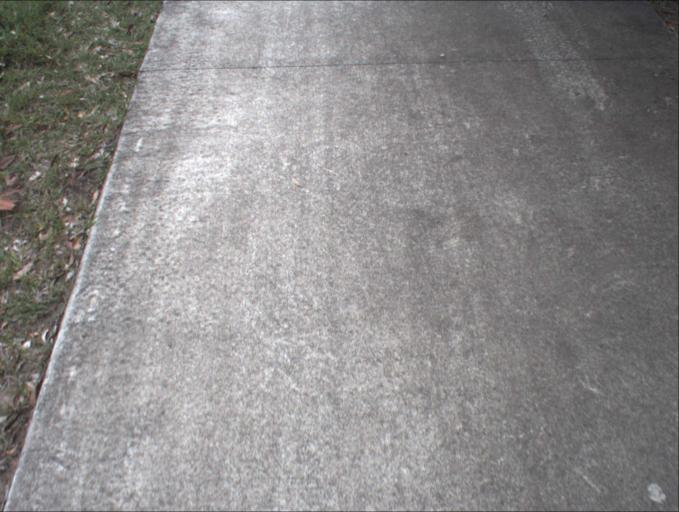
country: AU
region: Queensland
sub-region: Logan
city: Logan Reserve
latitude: -27.7083
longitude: 153.0754
